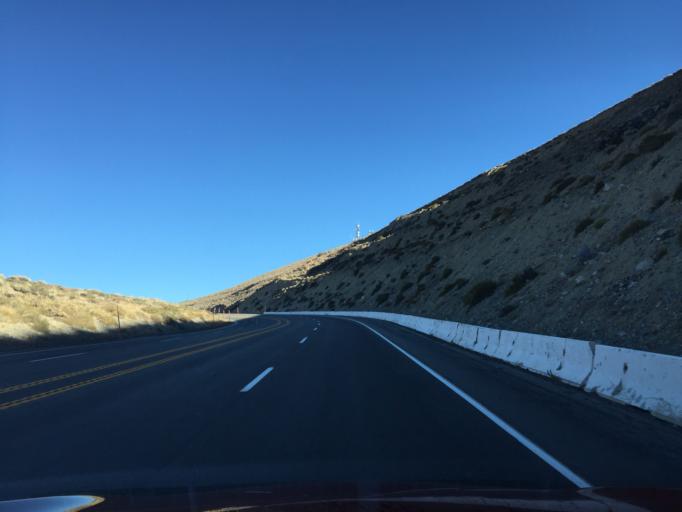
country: US
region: California
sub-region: Mono County
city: Bridgeport
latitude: 38.0816
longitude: -119.1781
